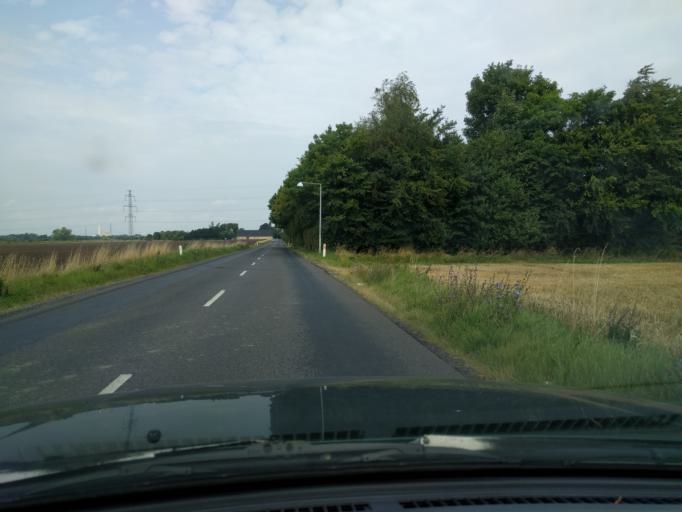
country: DK
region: South Denmark
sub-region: Odense Kommune
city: Neder Holluf
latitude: 55.3916
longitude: 10.4650
